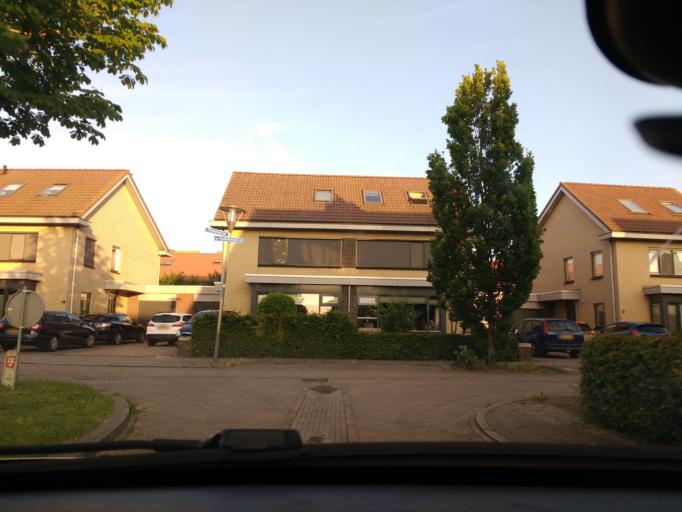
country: NL
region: Gelderland
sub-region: Gemeente Overbetuwe
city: Oosterhout
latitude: 51.8759
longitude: 5.8482
